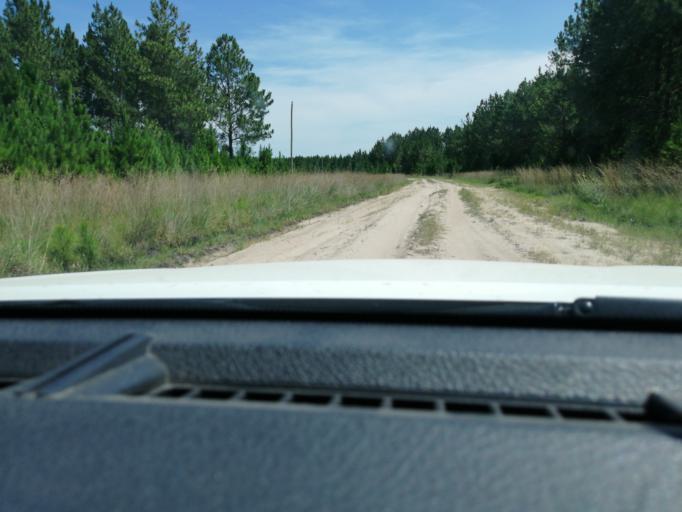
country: AR
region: Corrientes
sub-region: Departamento de San Miguel
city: San Miguel
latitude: -28.0255
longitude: -57.4775
